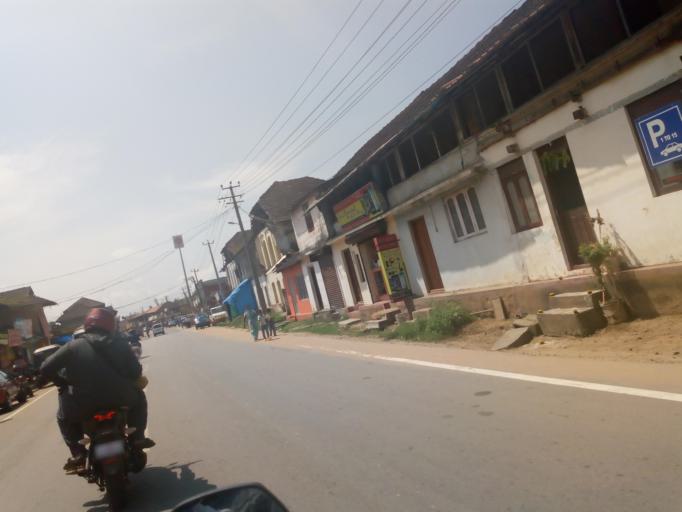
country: IN
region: Karnataka
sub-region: Kodagu
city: Ponnampet
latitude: 12.1441
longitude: 75.9445
